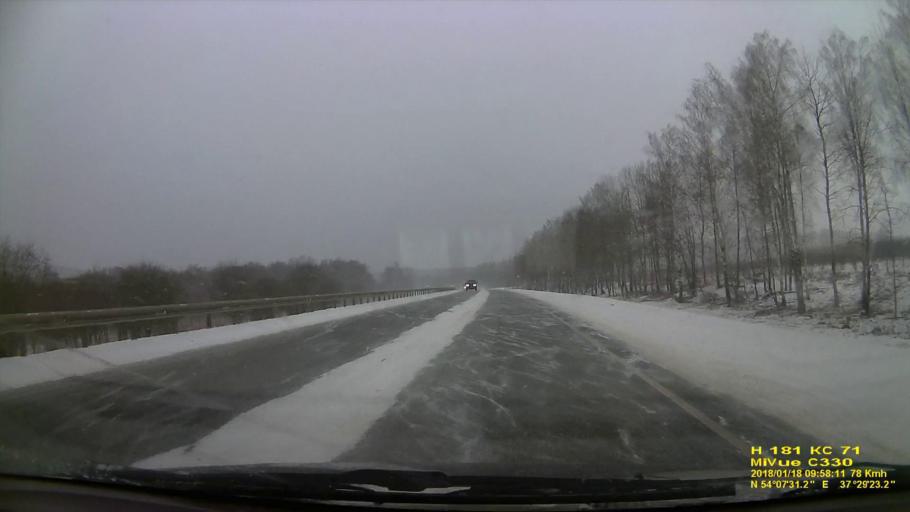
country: RU
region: Tula
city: Kosaya Gora
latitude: 54.1251
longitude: 37.4897
